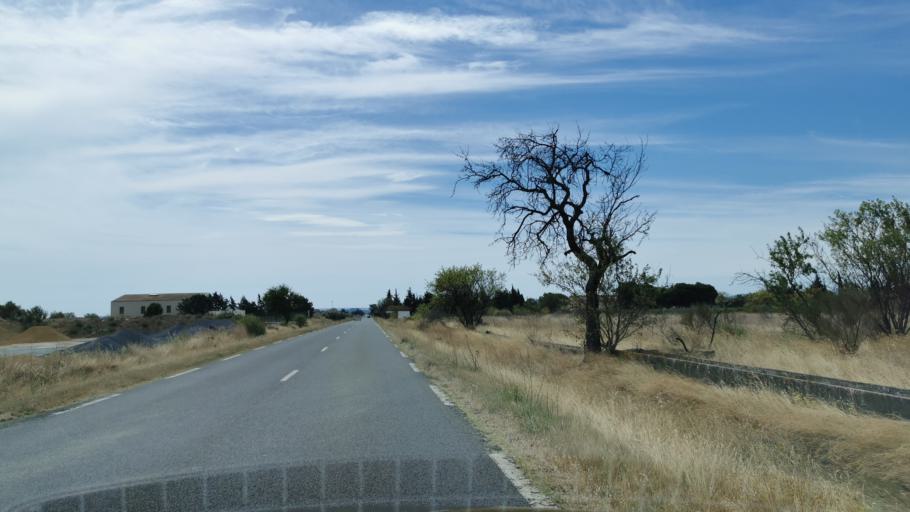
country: FR
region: Languedoc-Roussillon
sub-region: Departement de l'Aude
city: Ginestas
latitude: 43.2780
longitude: 2.8828
